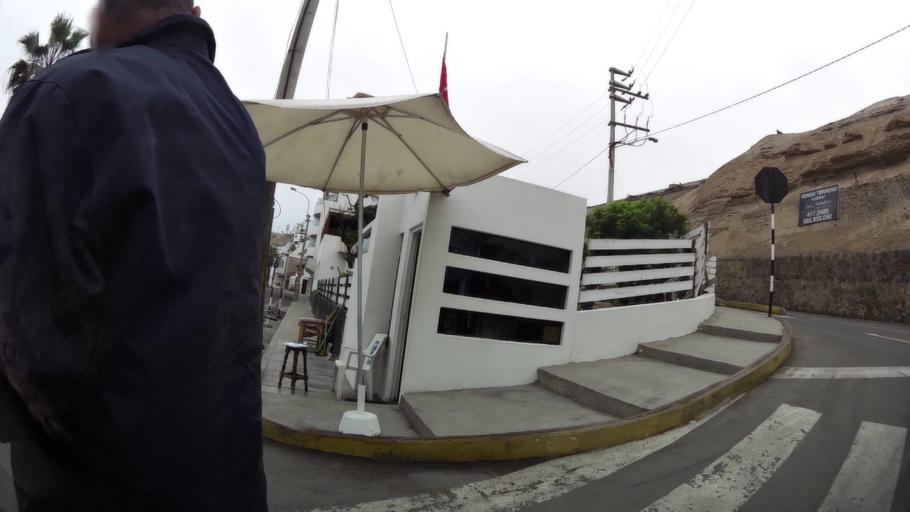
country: PE
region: Lima
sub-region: Lima
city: Punta Hermosa
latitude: -12.3392
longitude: -76.8183
